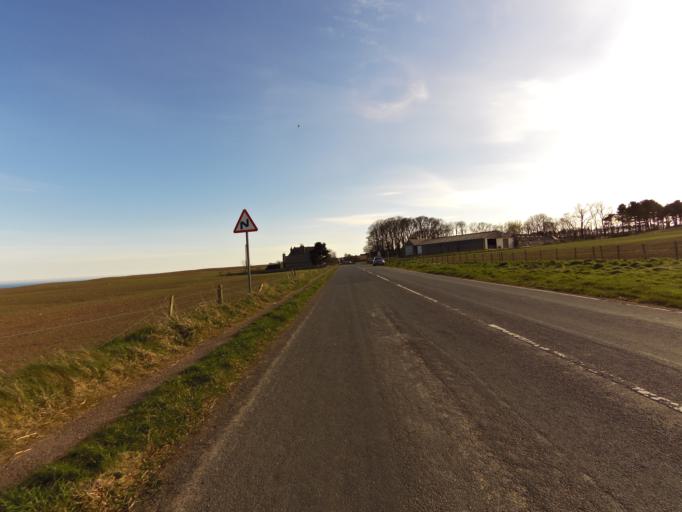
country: GB
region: Scotland
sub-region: Aberdeenshire
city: Stonehaven
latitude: 56.9467
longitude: -2.2055
